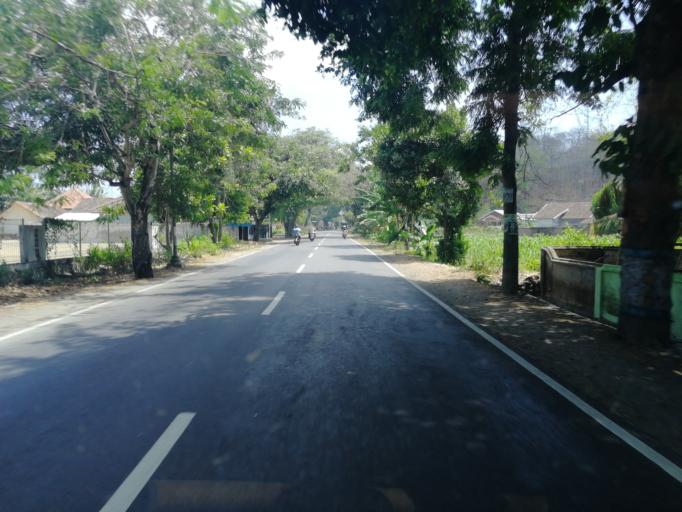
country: ID
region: West Nusa Tenggara
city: Jelateng Timur
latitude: -8.7103
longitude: 116.0772
